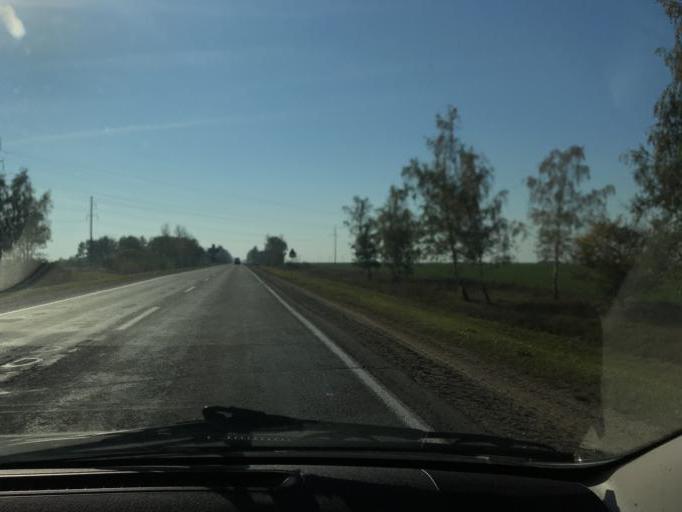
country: BY
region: Minsk
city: Salihorsk
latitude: 52.9068
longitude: 27.4781
